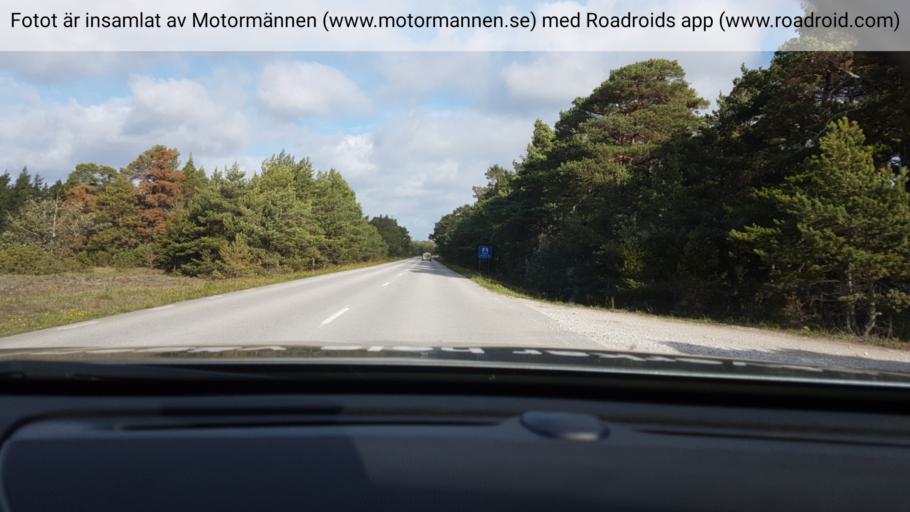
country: SE
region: Gotland
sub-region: Gotland
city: Slite
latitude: 57.8847
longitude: 19.0889
